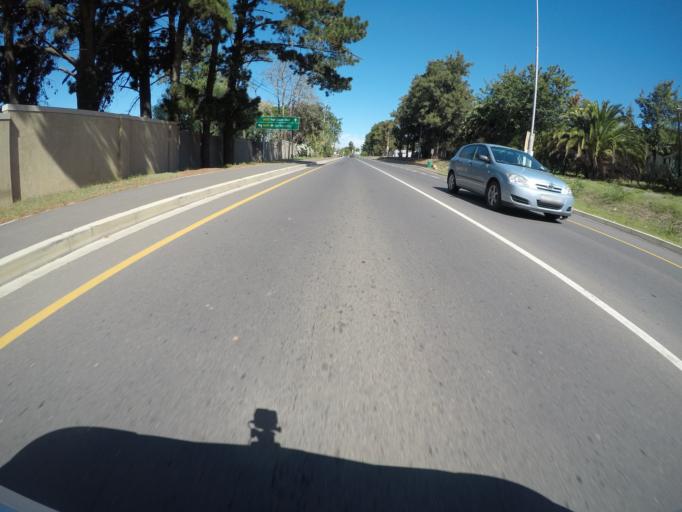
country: ZA
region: Western Cape
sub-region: City of Cape Town
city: Kraaifontein
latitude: -33.8268
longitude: 18.6370
